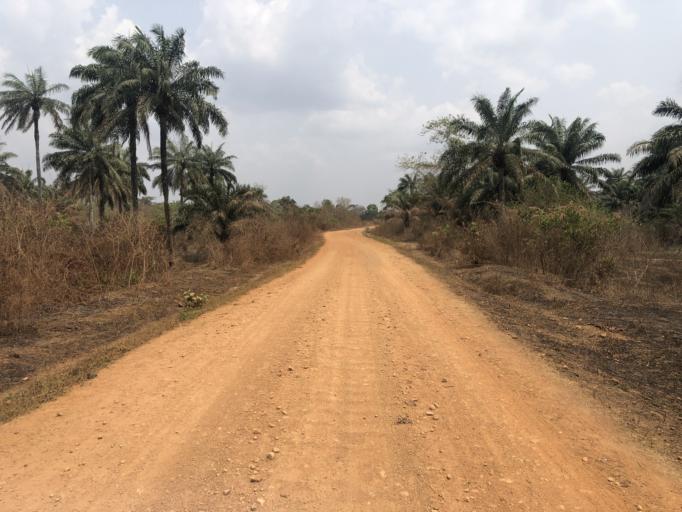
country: NG
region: Osun
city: Bode Osi
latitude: 7.7547
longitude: 4.2378
